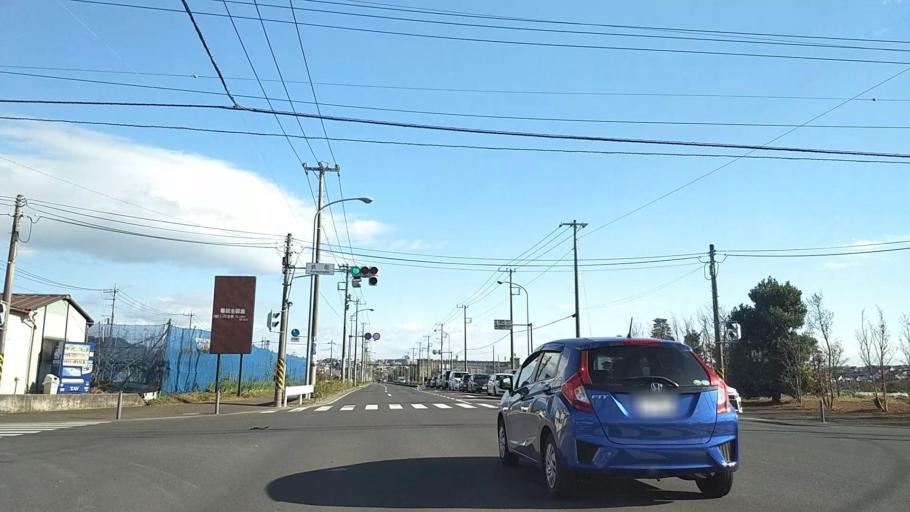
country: JP
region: Tokyo
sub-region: Machida-shi
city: Machida
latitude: 35.5599
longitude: 139.5243
